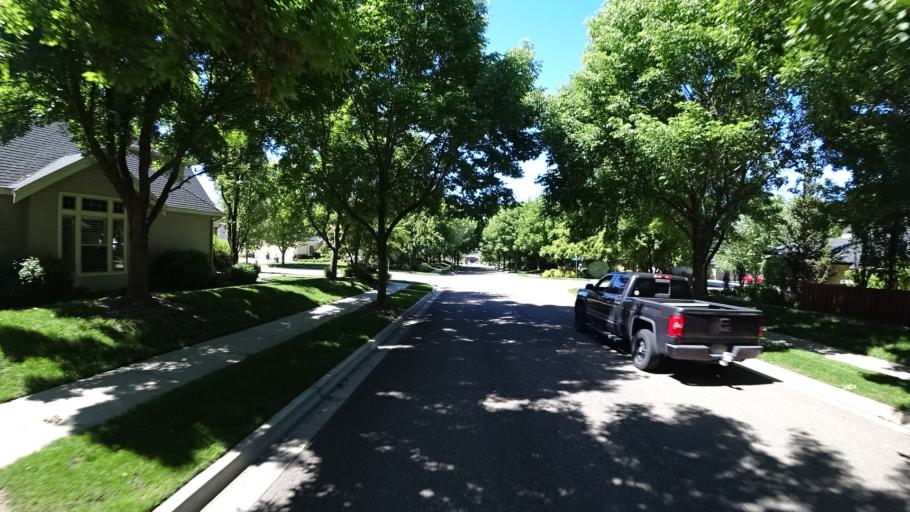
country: US
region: Idaho
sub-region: Ada County
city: Boise
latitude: 43.5714
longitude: -116.1173
